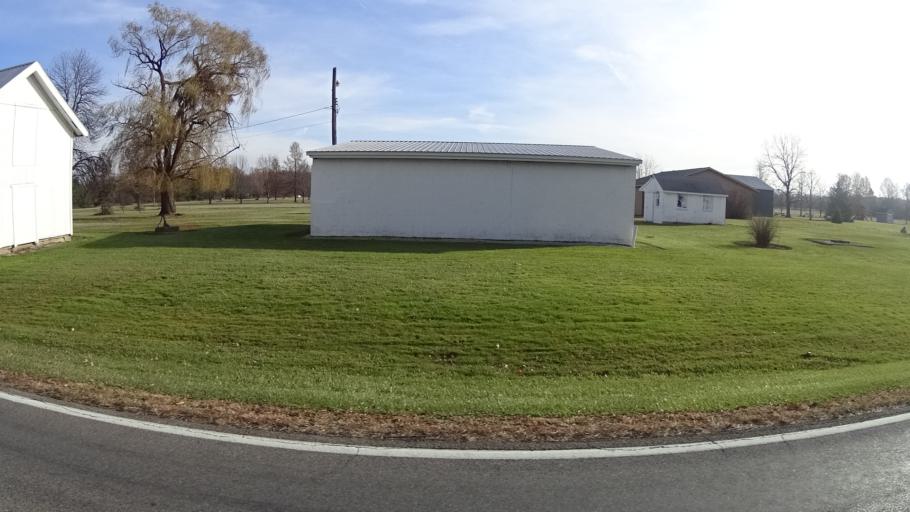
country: US
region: Ohio
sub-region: Lorain County
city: Eaton Estates
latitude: 41.2592
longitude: -81.9827
